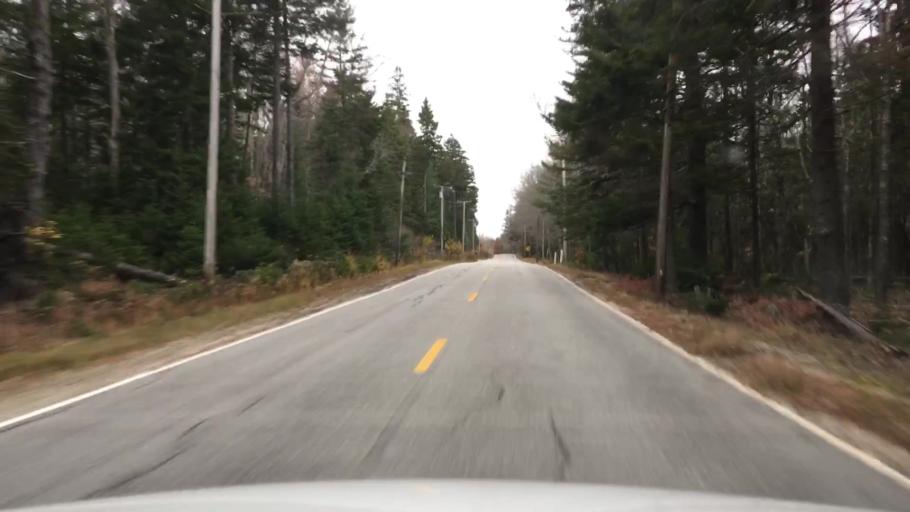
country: US
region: Maine
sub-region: Hancock County
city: Sedgwick
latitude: 44.2979
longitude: -68.5580
